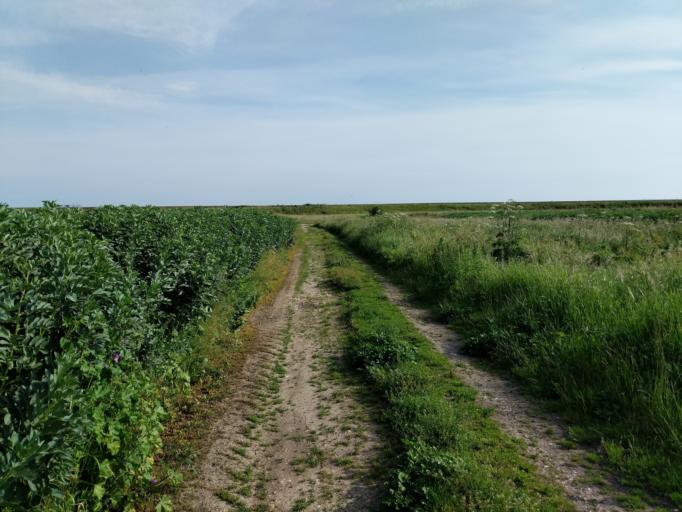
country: GB
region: England
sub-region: Kent
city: Faversham
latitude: 51.3421
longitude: 0.9103
